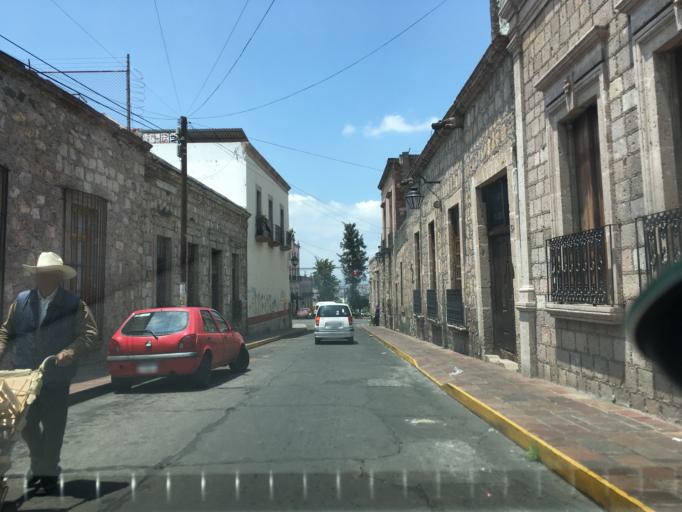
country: MX
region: Michoacan
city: Morelia
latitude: 19.7043
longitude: -101.1983
